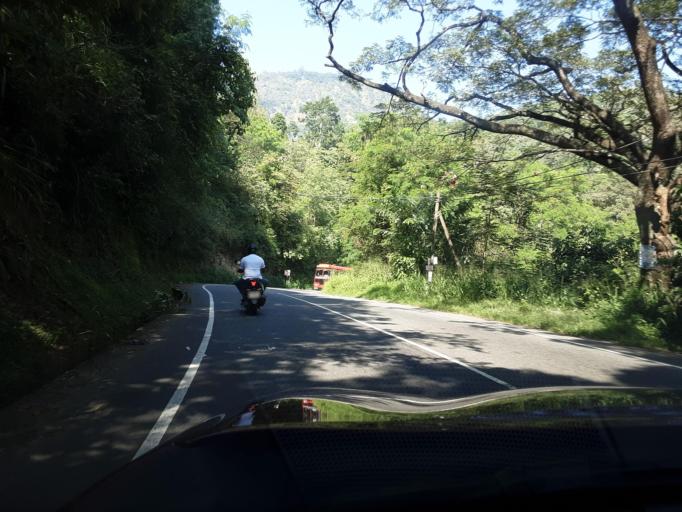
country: LK
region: Uva
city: Badulla
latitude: 7.0399
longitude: 81.0602
